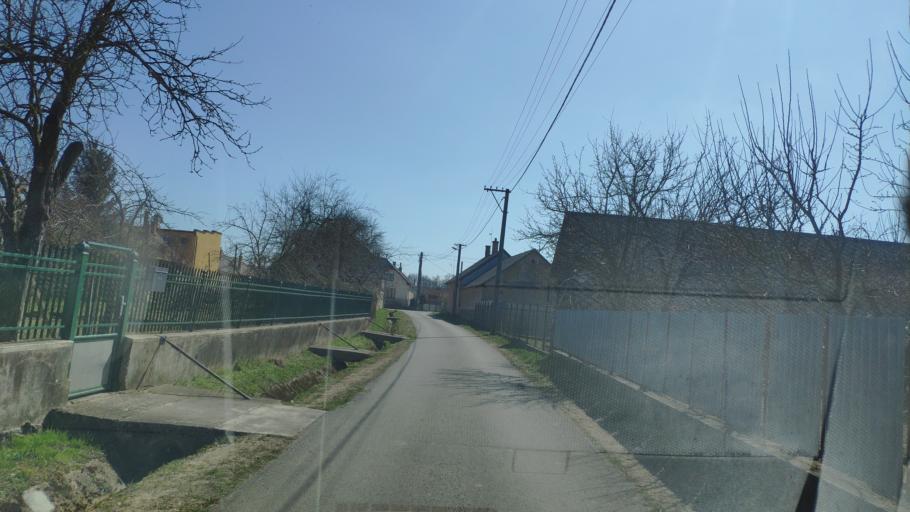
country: SK
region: Kosicky
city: Moldava nad Bodvou
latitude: 48.5792
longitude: 20.9497
